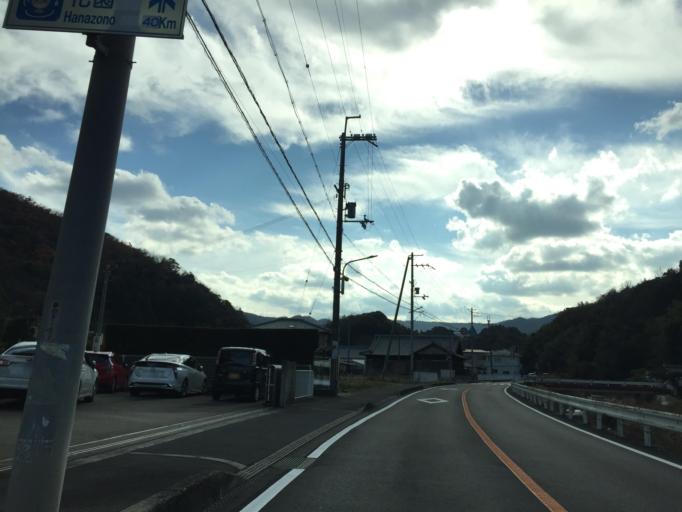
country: JP
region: Wakayama
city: Kainan
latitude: 34.1698
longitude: 135.2508
